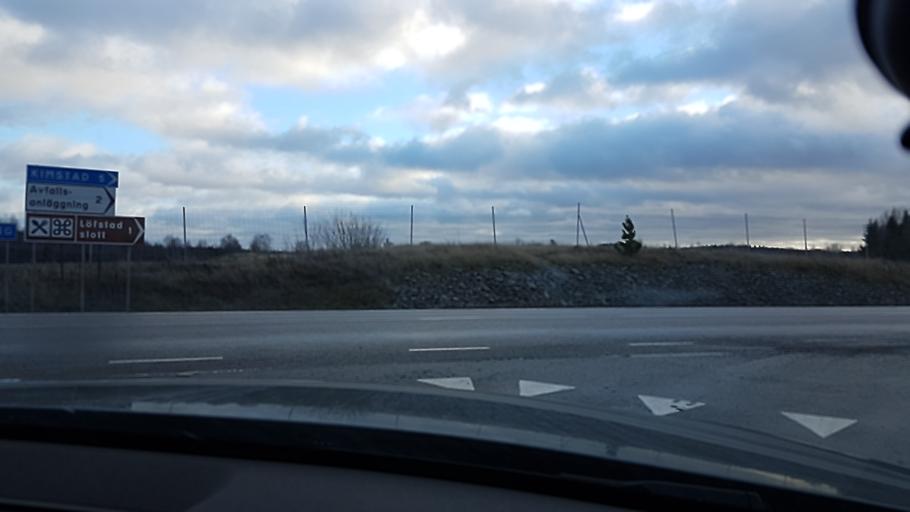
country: SE
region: OEstergoetland
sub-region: Norrkopings Kommun
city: Kimstad
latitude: 58.5524
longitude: 16.0571
